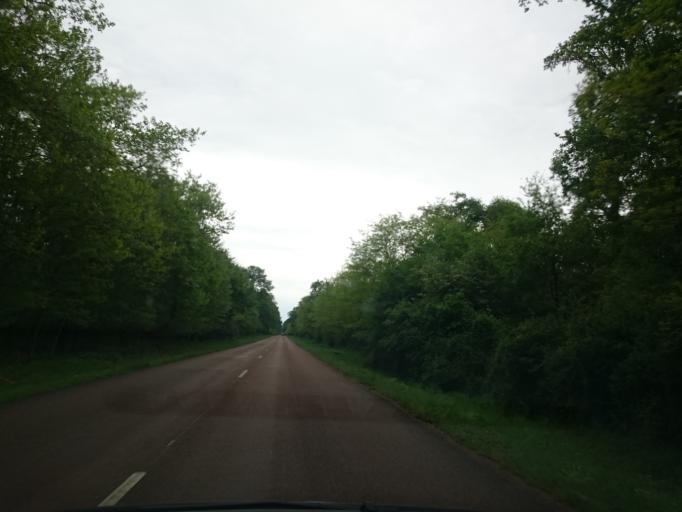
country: FR
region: Centre
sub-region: Departement du Loir-et-Cher
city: Muides-sur-Loire
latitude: 47.6442
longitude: 1.5249
